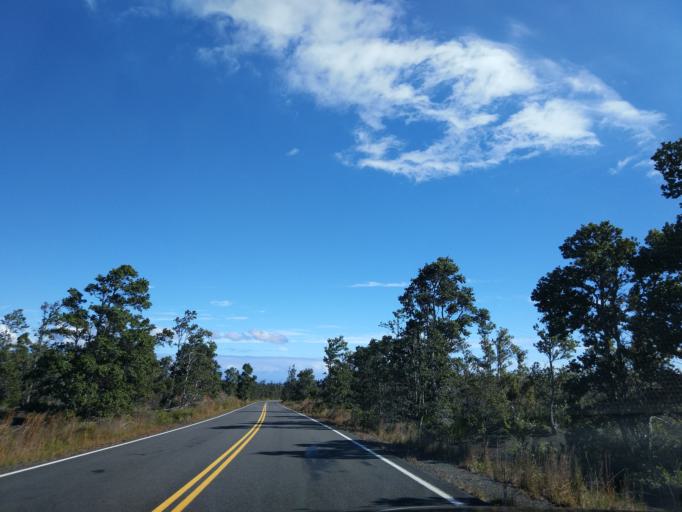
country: US
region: Hawaii
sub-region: Hawaii County
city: Volcano
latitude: 19.3418
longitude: -155.2110
